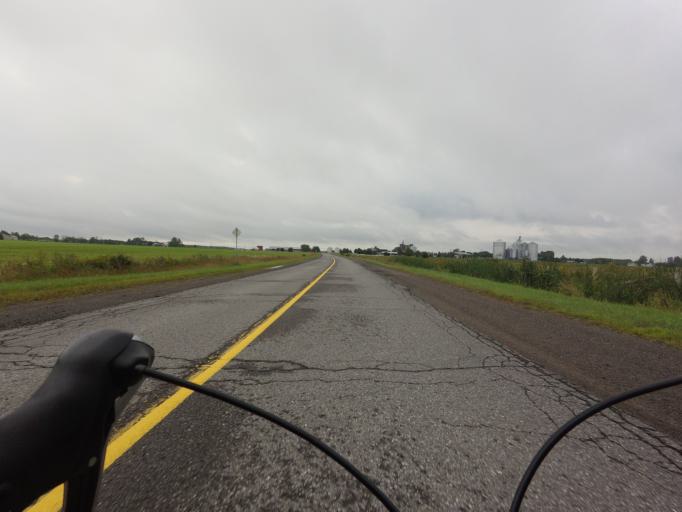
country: CA
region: Ontario
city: Bells Corners
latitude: 45.1431
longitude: -75.7770
